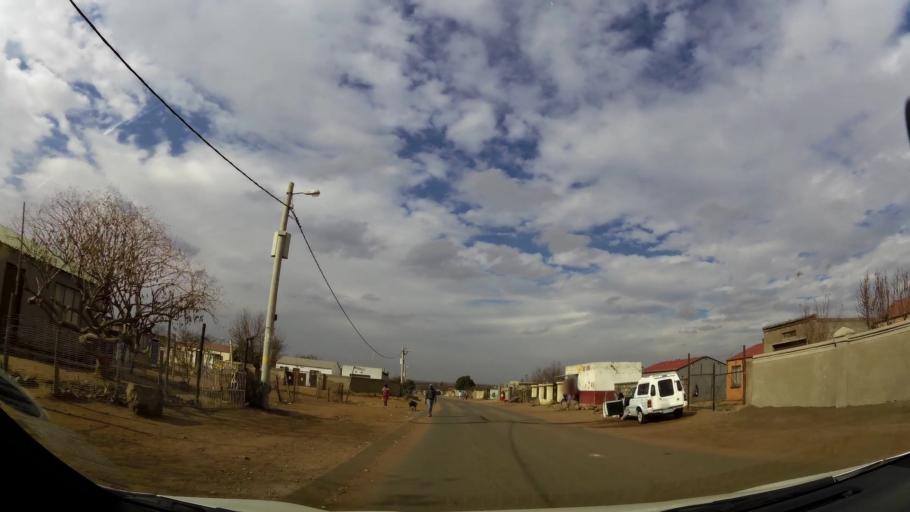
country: ZA
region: Gauteng
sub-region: Ekurhuleni Metropolitan Municipality
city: Germiston
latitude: -26.4018
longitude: 28.1582
